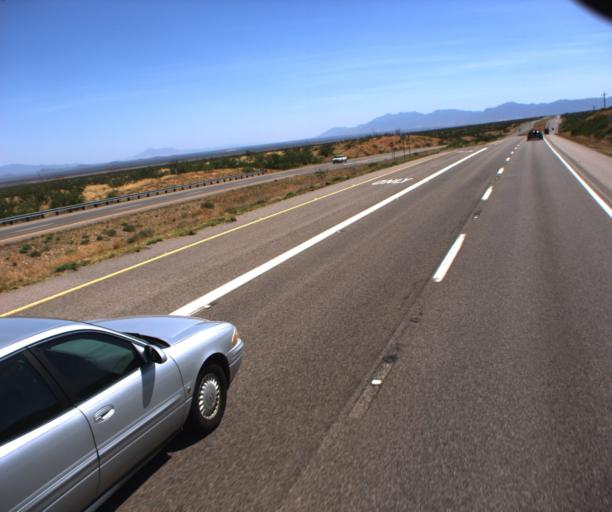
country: US
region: Arizona
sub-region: Cochise County
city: Whetstone
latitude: 31.8453
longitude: -110.3419
